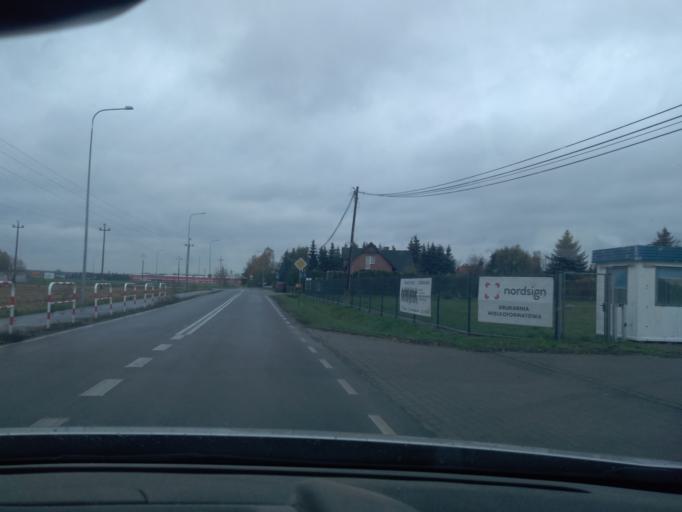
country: PL
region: Greater Poland Voivodeship
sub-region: Powiat obornicki
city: Oborniki
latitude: 52.6507
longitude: 16.8468
